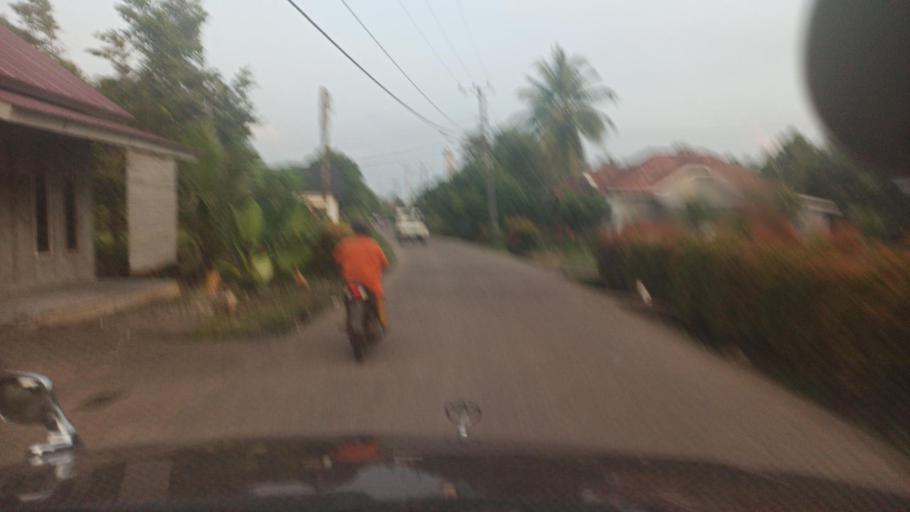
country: ID
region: South Sumatra
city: Prabumulih
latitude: -3.3002
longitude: 104.1462
